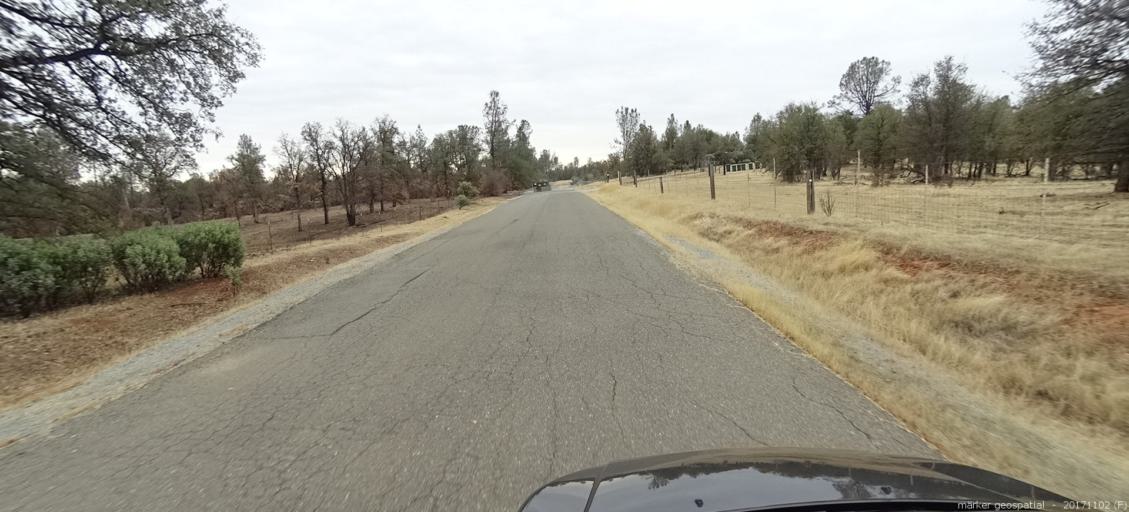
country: US
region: California
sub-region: Shasta County
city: Bella Vista
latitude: 40.6109
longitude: -122.2964
